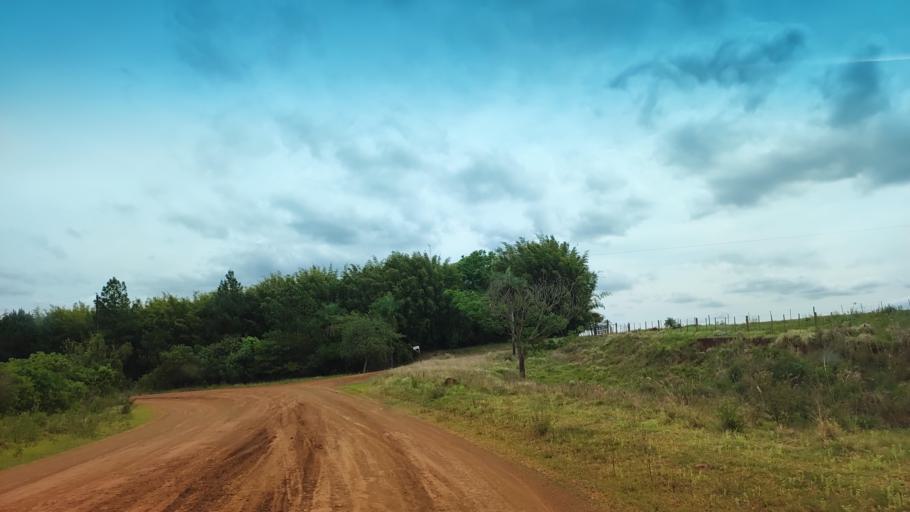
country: AR
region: Misiones
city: Garupa
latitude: -27.5167
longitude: -55.9743
